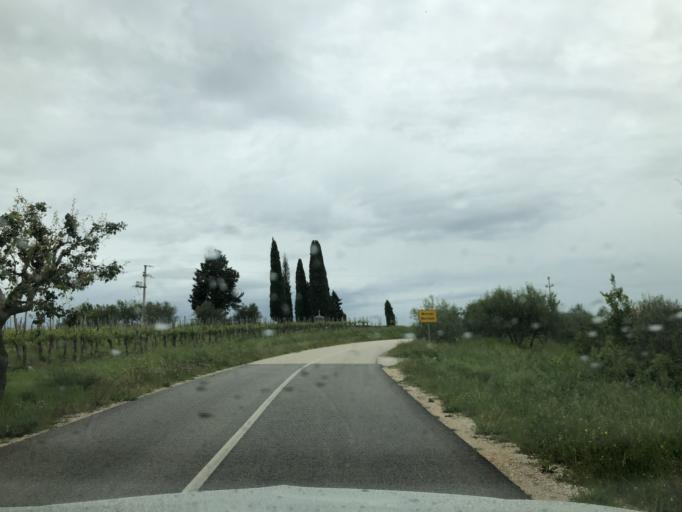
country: HR
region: Istarska
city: Buje
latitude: 45.4371
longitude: 13.7046
